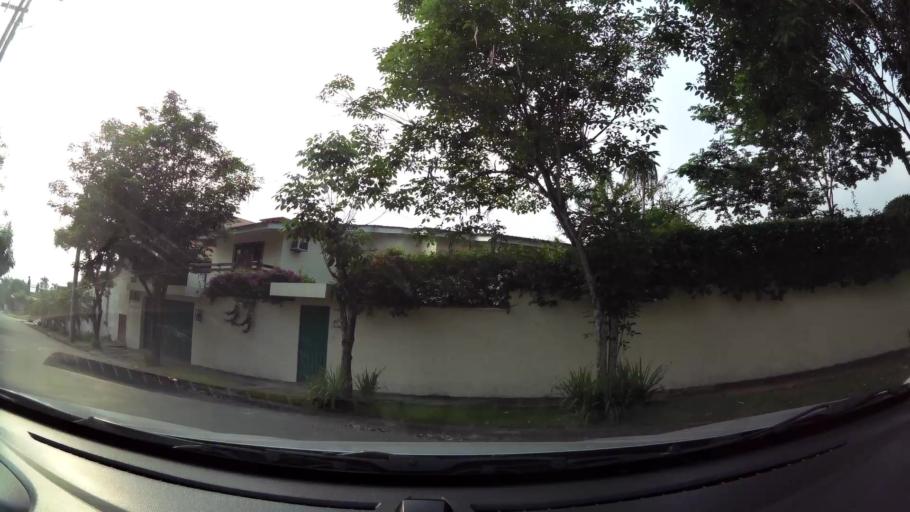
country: HN
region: Cortes
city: Armenta
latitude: 15.4926
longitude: -88.0477
